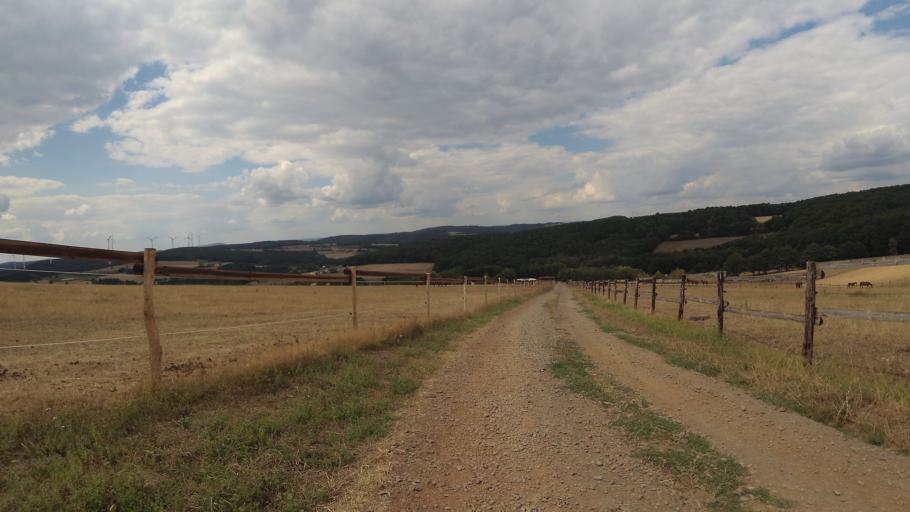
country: DE
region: Rheinland-Pfalz
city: Breitenbach
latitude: 49.4314
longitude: 7.2527
